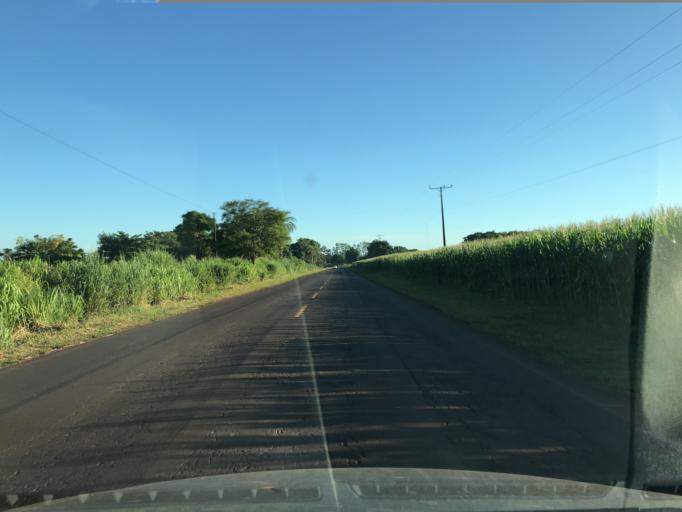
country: BR
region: Parana
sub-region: Ipora
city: Ipora
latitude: -24.0932
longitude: -53.8359
